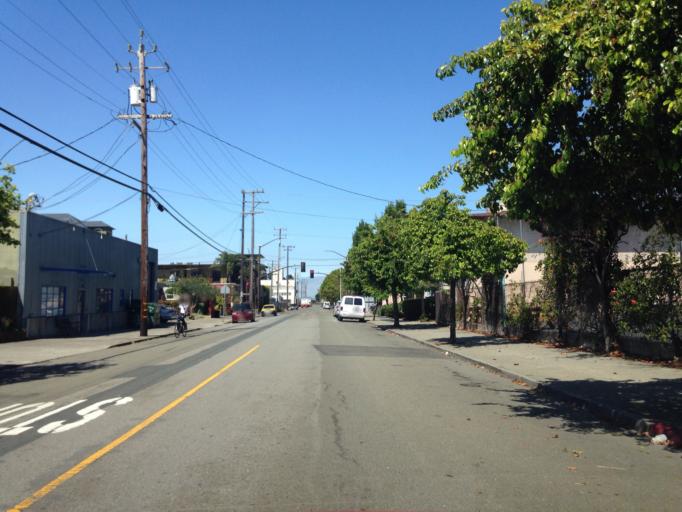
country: US
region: California
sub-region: Alameda County
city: Berkeley
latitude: 37.8555
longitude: -122.2914
